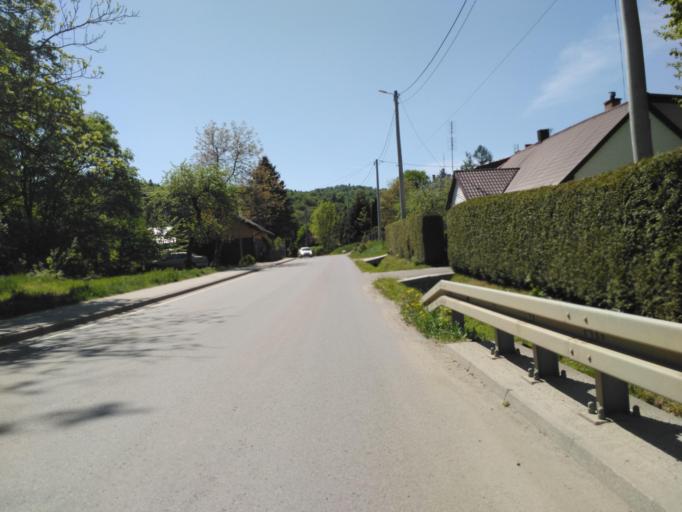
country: PL
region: Subcarpathian Voivodeship
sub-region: Powiat krosnienski
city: Iwonicz-Zdroj
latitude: 49.5701
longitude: 21.7928
